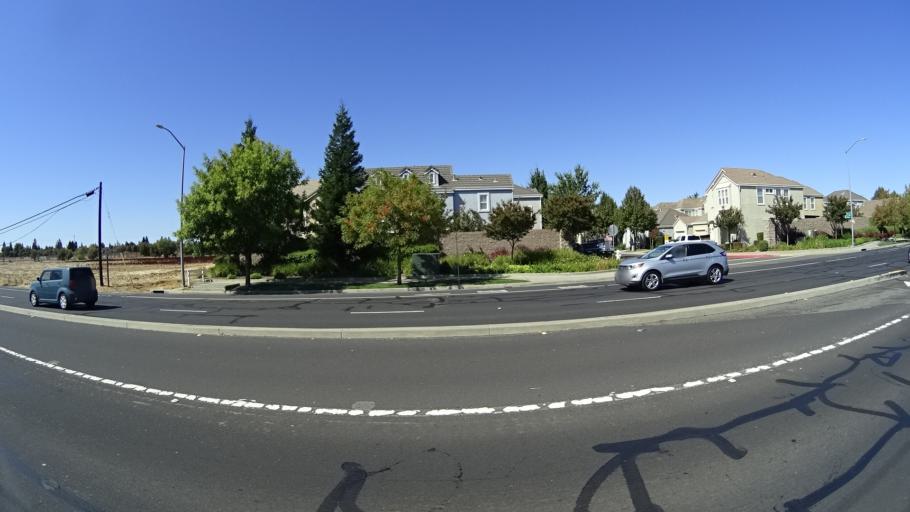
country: US
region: California
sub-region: Sacramento County
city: Elk Grove
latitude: 38.4362
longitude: -121.3715
